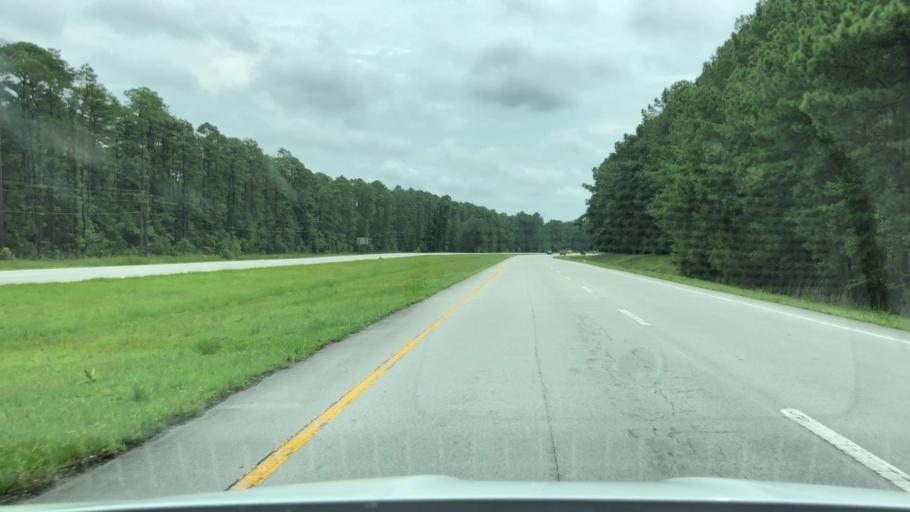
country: US
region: North Carolina
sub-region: Craven County
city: Havelock
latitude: 34.8476
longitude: -76.8855
